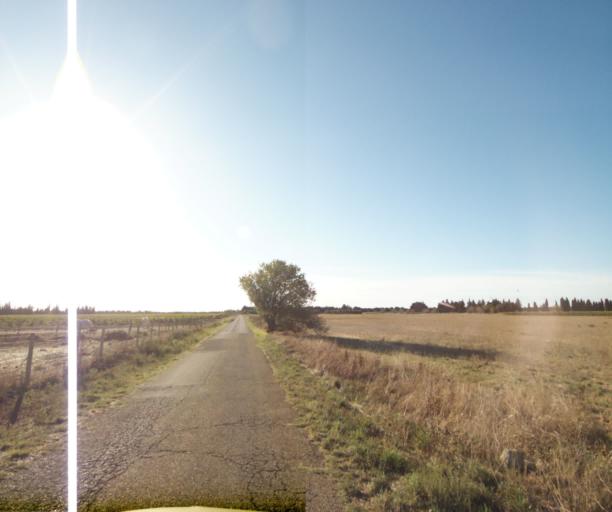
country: FR
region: Languedoc-Roussillon
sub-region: Departement du Gard
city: Garons
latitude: 43.7807
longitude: 4.4583
